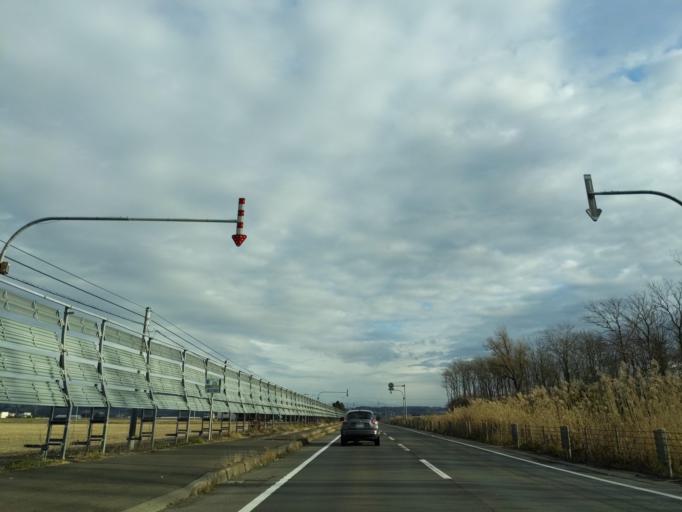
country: JP
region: Hokkaido
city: Kitahiroshima
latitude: 42.9616
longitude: 141.6864
